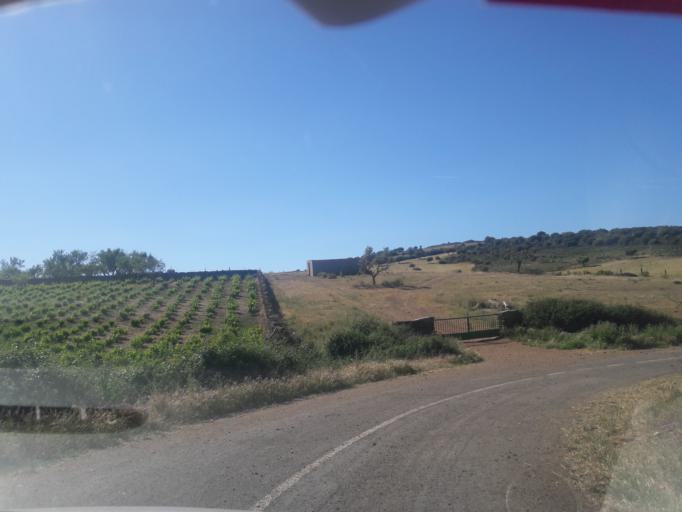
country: ES
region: Castille and Leon
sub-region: Provincia de Salamanca
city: Saucelle
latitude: 41.0404
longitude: -6.7597
